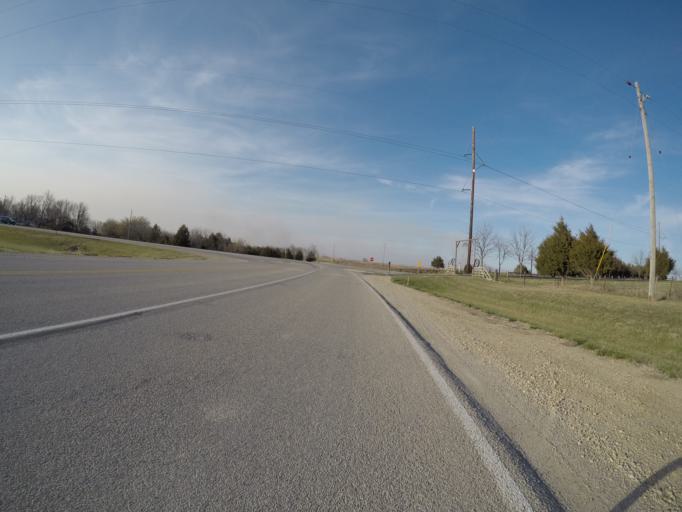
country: US
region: Kansas
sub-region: Riley County
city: Manhattan
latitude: 39.2513
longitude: -96.6534
